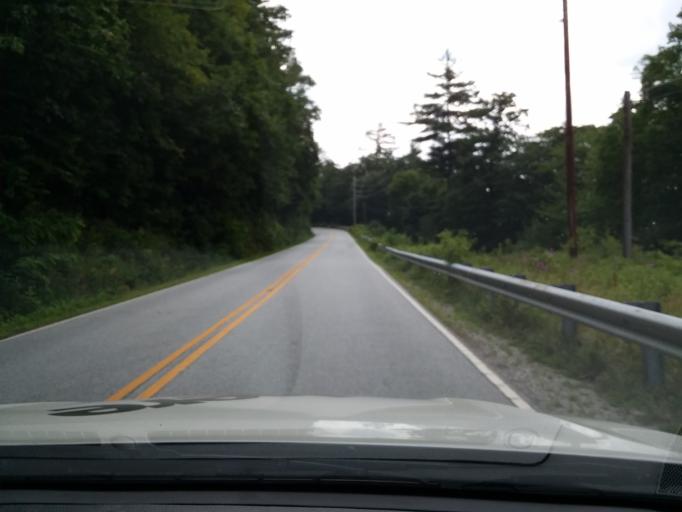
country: US
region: Georgia
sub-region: Rabun County
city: Mountain City
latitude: 35.0284
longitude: -83.2801
